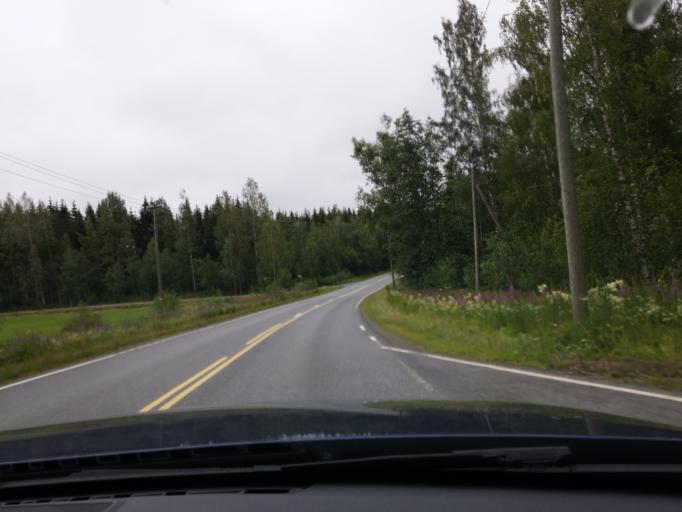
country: FI
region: Central Finland
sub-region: Joutsa
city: Joutsa
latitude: 61.8106
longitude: 25.9676
